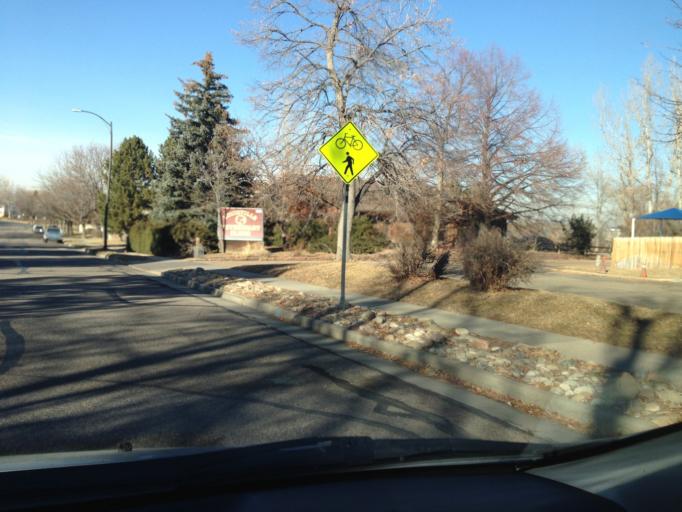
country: US
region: Colorado
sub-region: Boulder County
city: Louisville
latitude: 39.9891
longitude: -105.1345
